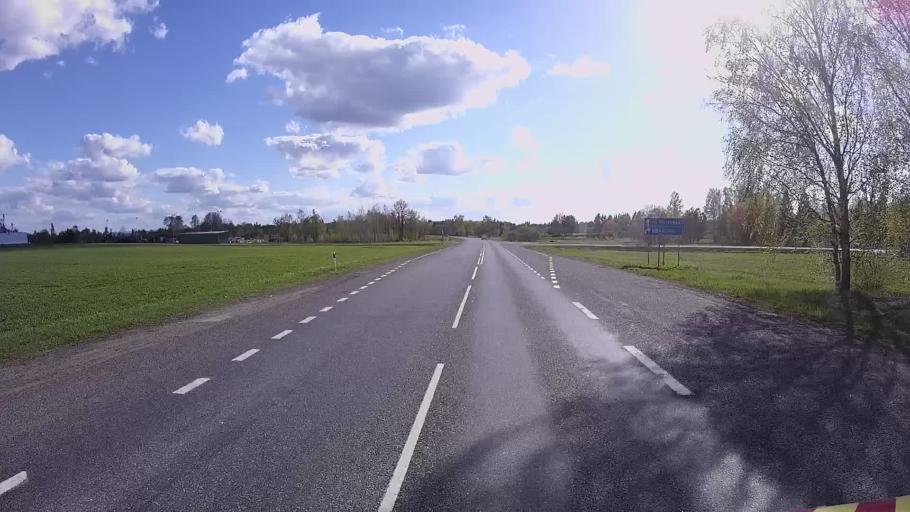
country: EE
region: Jogevamaa
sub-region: Poltsamaa linn
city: Poltsamaa
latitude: 58.6700
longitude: 25.9967
